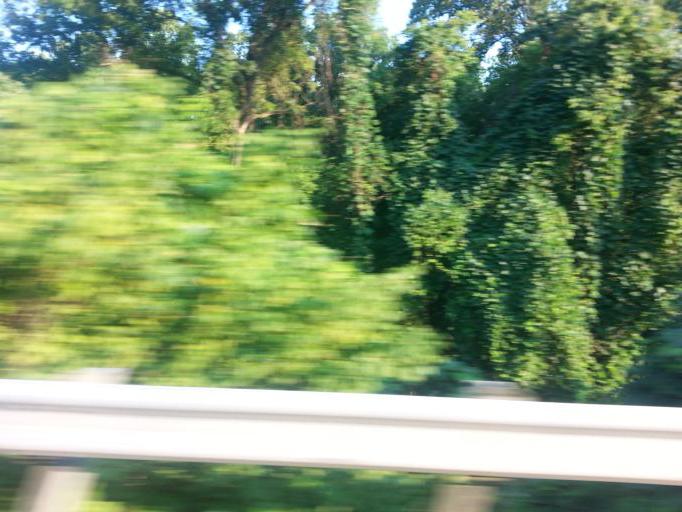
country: US
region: Tennessee
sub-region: Anderson County
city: Clinton
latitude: 36.0273
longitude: -84.0763
